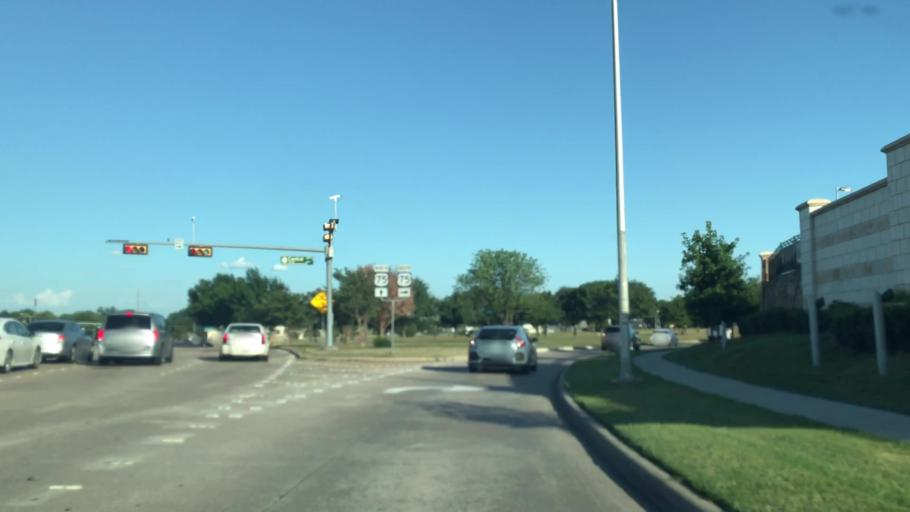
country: US
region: Texas
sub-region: Collin County
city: Allen
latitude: 33.0668
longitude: -96.6920
